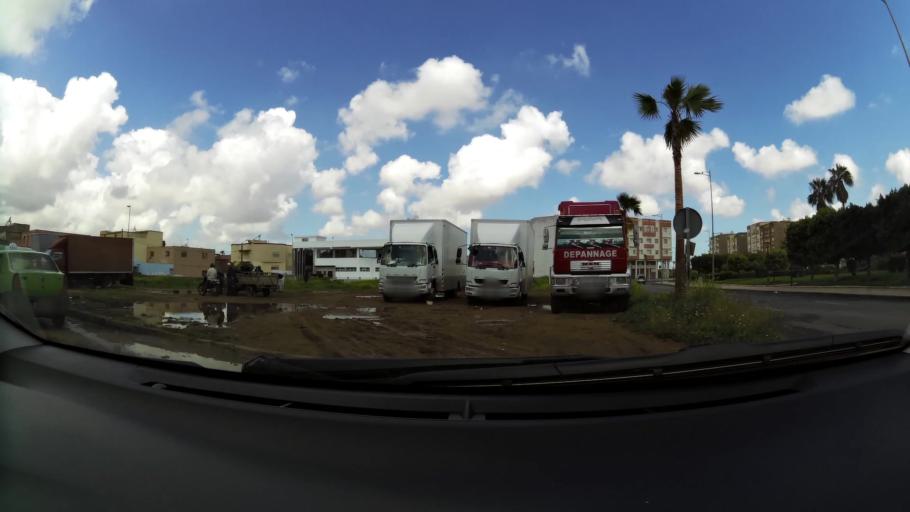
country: MA
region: Grand Casablanca
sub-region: Mediouna
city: Tit Mellil
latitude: 33.5531
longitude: -7.4849
